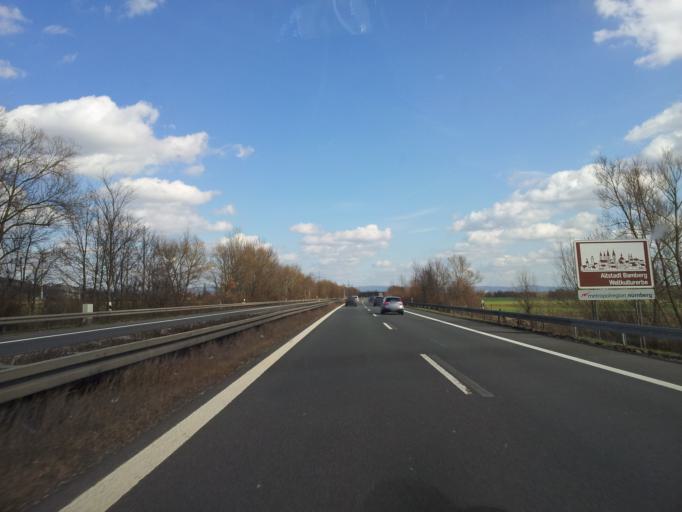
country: DE
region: Bavaria
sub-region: Upper Franconia
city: Oberhaid
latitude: 49.9270
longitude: 10.8030
